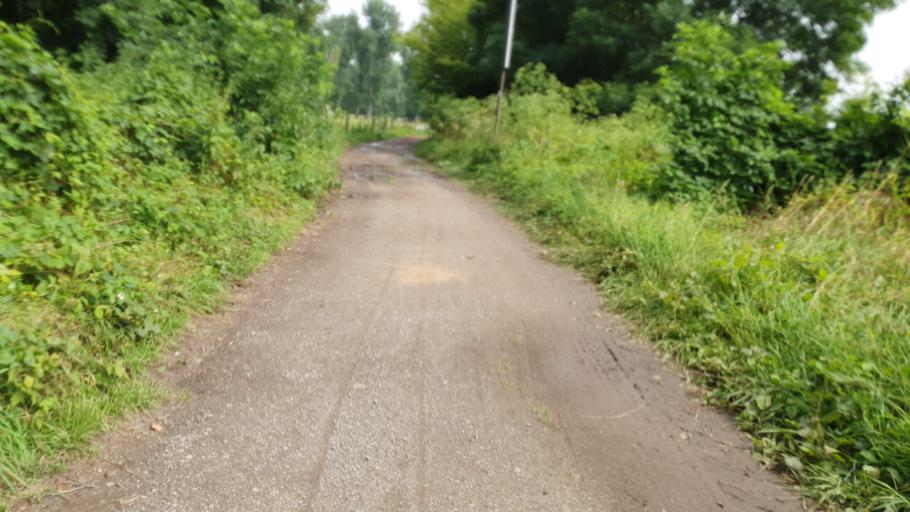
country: DE
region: North Rhine-Westphalia
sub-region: Regierungsbezirk Dusseldorf
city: Dormagen
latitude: 51.1387
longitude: 6.8453
